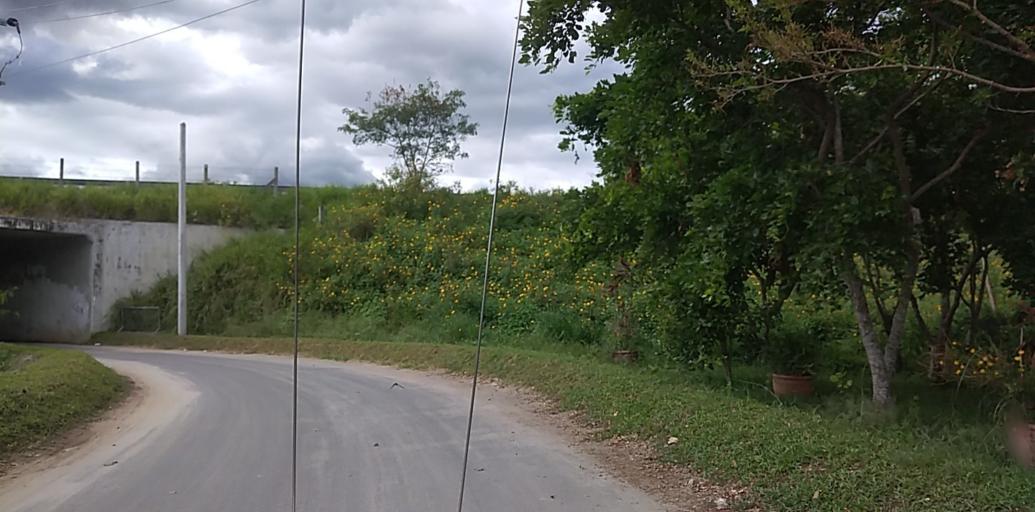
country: PH
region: Central Luzon
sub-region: Province of Pampanga
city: Dolores
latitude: 15.1156
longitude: 120.5059
